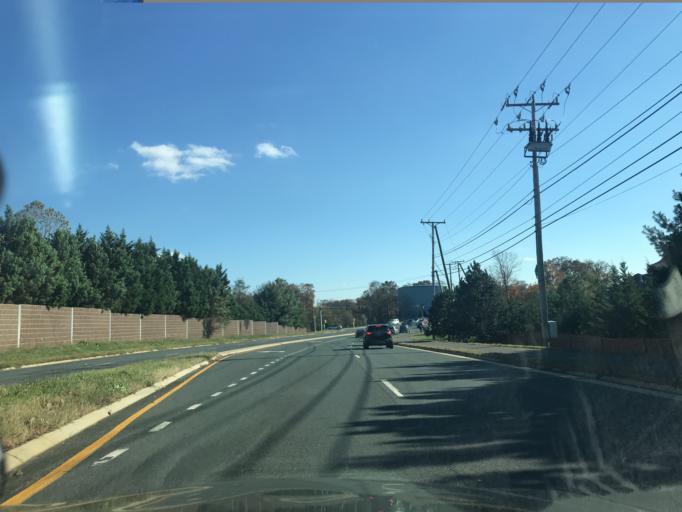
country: US
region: Virginia
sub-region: Fairfax County
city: Greenbriar
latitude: 38.8820
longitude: -77.3706
